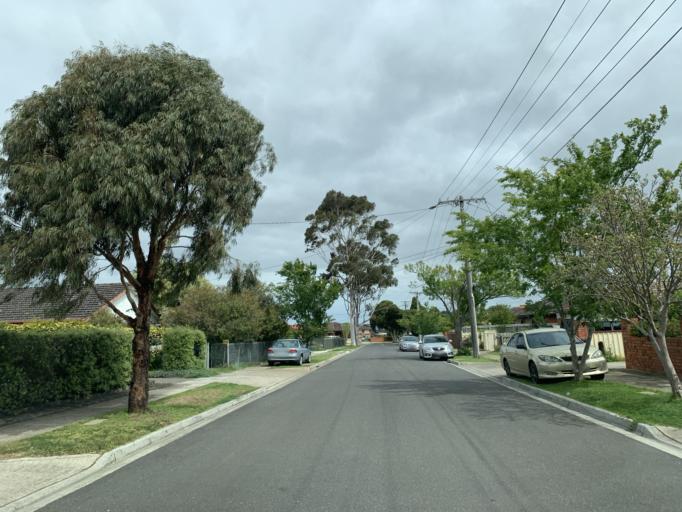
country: AU
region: Victoria
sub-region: Brimbank
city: Kealba
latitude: -37.7402
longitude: 144.8179
